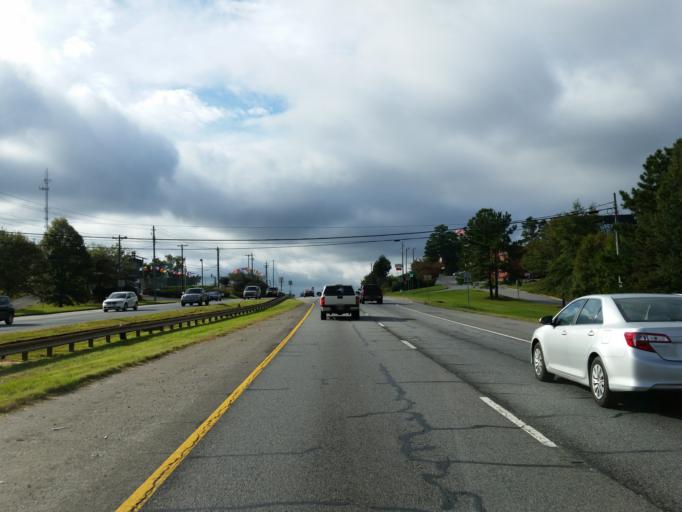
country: US
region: Georgia
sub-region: Cobb County
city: Marietta
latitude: 33.9821
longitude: -84.5601
